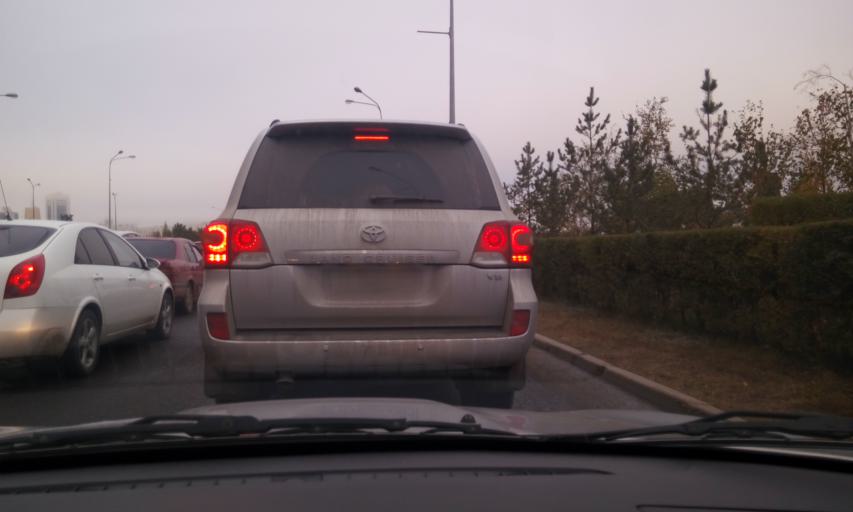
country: KZ
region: Astana Qalasy
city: Astana
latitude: 51.1294
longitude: 71.4599
